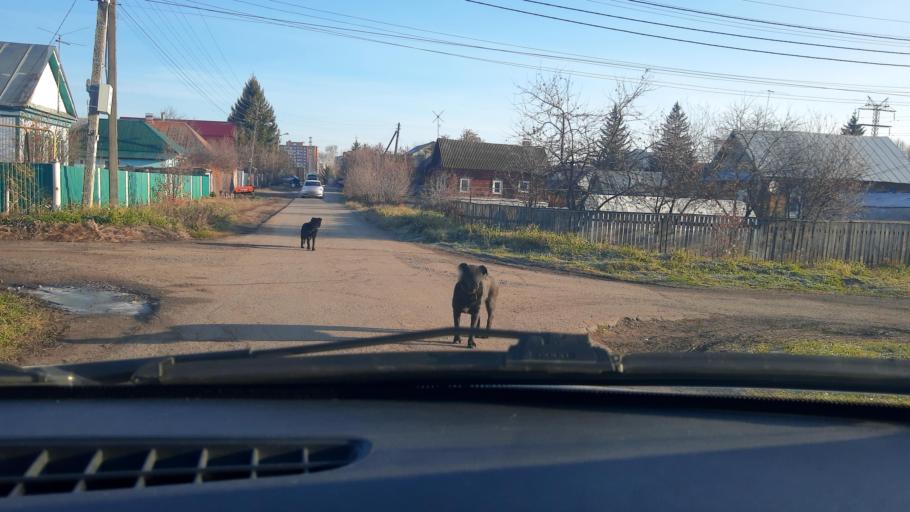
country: RU
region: Bashkortostan
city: Avdon
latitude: 54.6914
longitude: 55.8109
